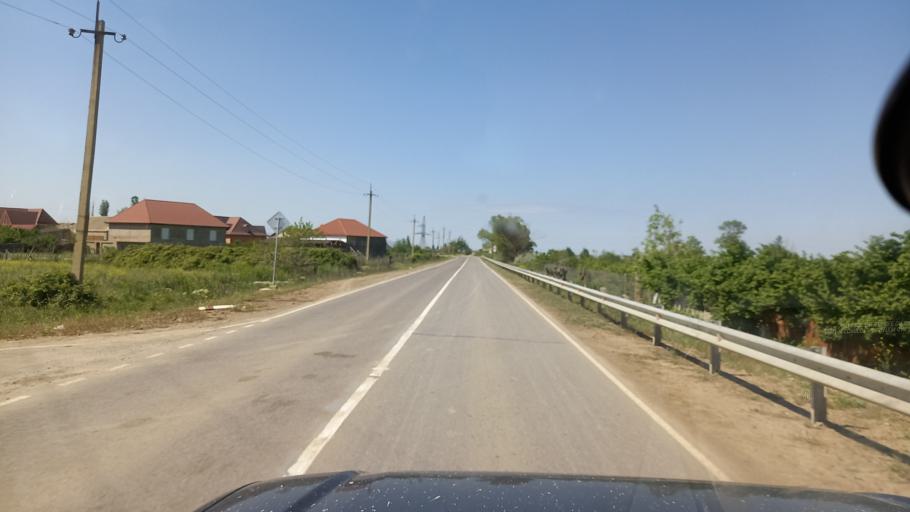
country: RU
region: Dagestan
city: Novaya Maka
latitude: 41.8225
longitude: 48.4003
